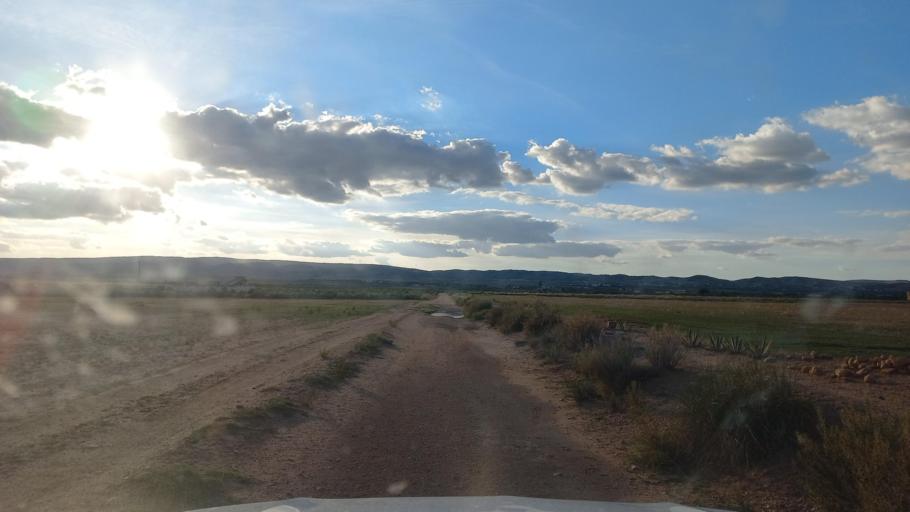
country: TN
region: Al Qasrayn
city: Sbiba
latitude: 35.3509
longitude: 9.0389
